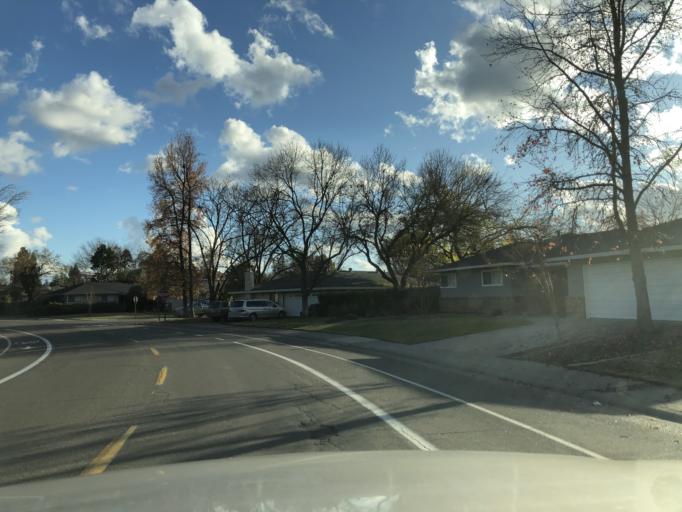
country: US
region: California
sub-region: Sacramento County
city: Foothill Farms
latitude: 38.6580
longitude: -121.3216
